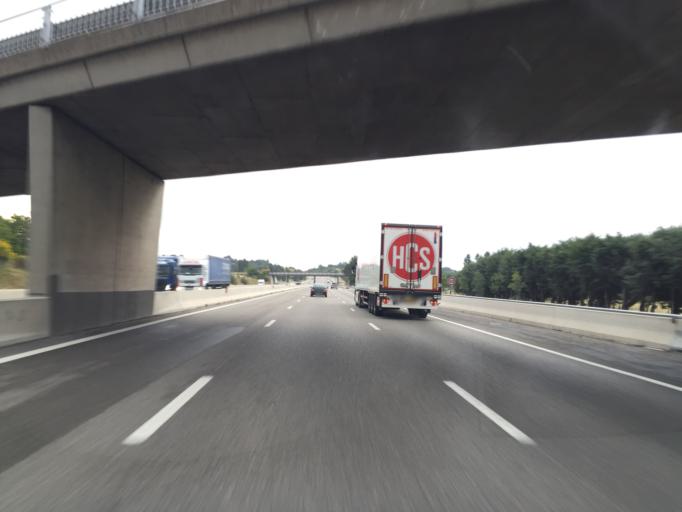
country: FR
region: Provence-Alpes-Cote d'Azur
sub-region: Departement du Var
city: Saint-Maximin-la-Sainte-Baume
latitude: 43.4537
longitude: 5.8788
